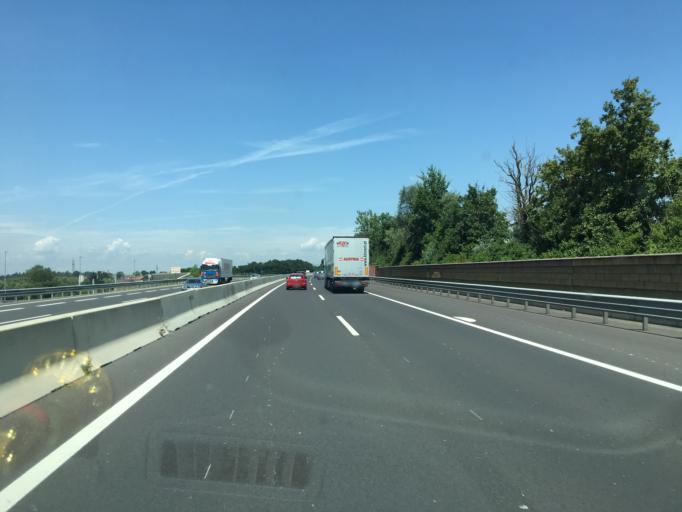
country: AT
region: Styria
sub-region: Politischer Bezirk Leibnitz
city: Weitendorf
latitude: 46.8890
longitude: 15.4727
